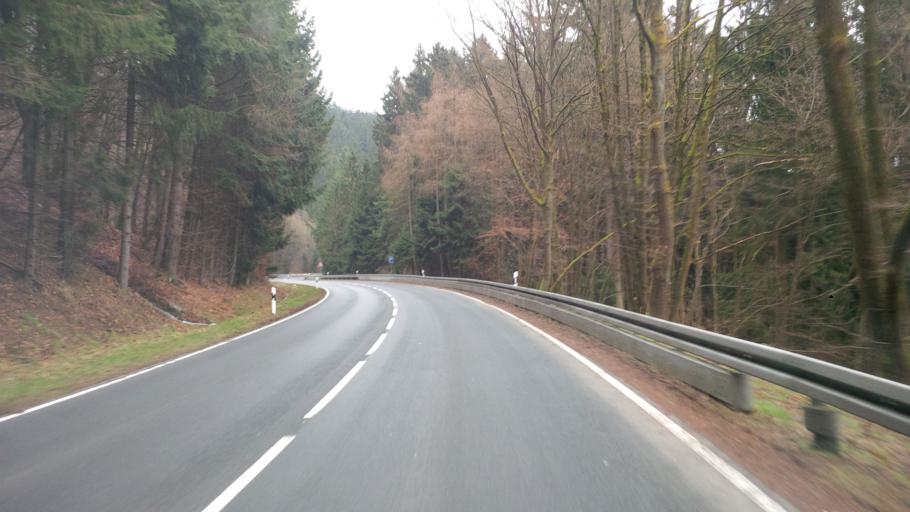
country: DE
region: Hesse
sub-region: Regierungsbezirk Darmstadt
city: Kronberg
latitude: 50.2296
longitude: 8.5095
